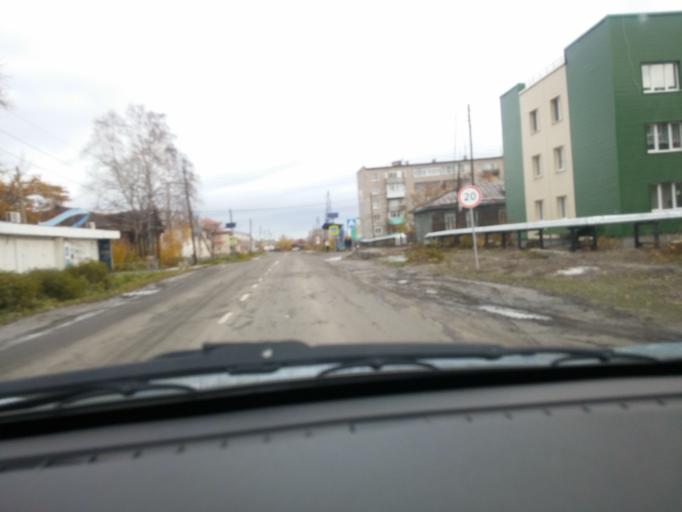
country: RU
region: Sverdlovsk
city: Turinsk
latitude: 58.0396
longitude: 63.7063
